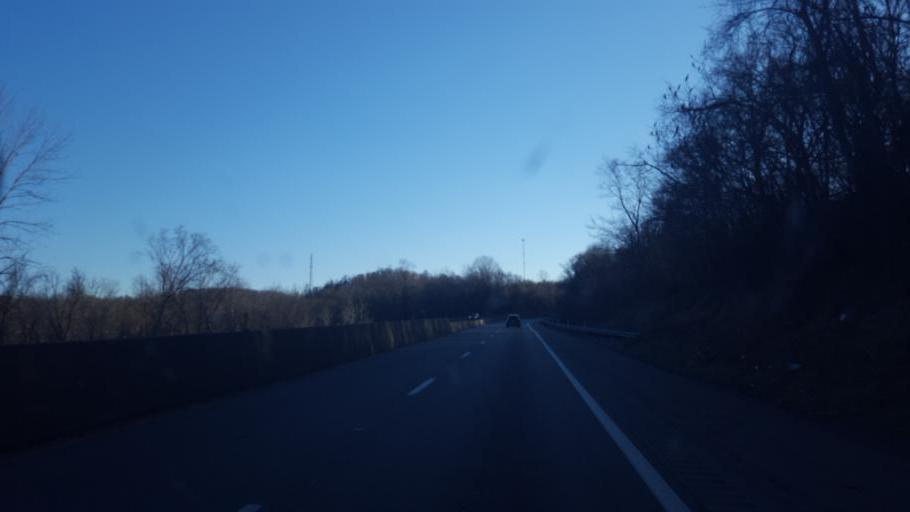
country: US
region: Pennsylvania
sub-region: Westmoreland County
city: New Stanton
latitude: 40.1950
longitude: -79.6859
